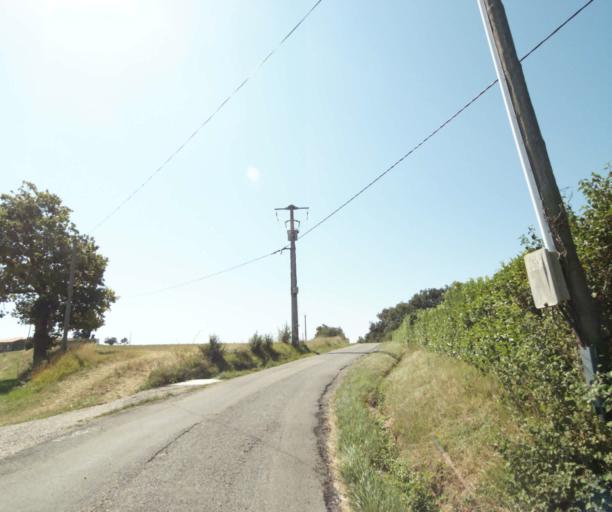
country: FR
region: Midi-Pyrenees
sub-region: Departement de l'Ariege
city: Lezat-sur-Leze
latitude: 43.2732
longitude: 1.3759
